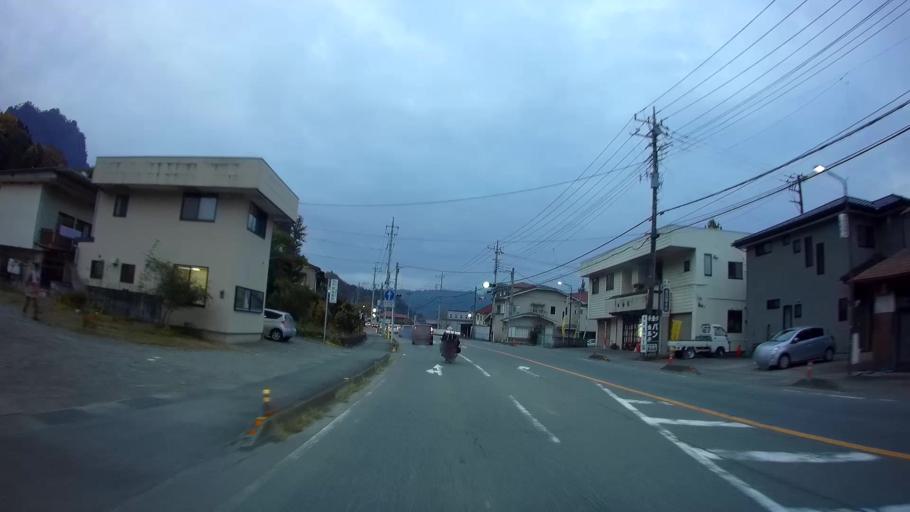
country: JP
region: Gunma
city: Nakanojomachi
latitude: 36.5516
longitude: 138.7837
